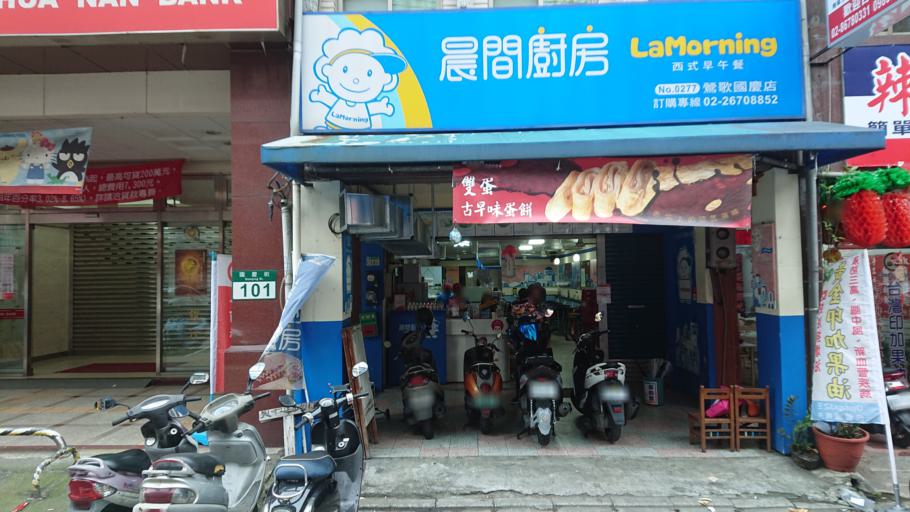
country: TW
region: Taiwan
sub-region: Taoyuan
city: Taoyuan
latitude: 24.9544
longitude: 121.3505
